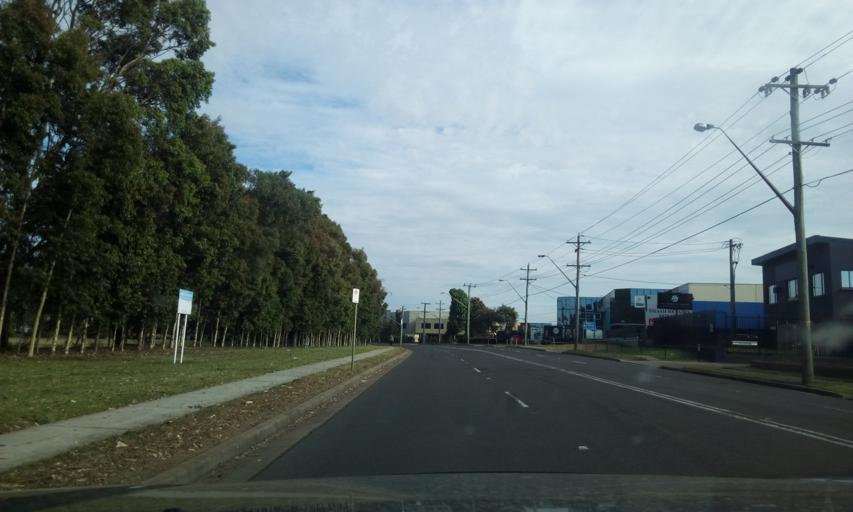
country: AU
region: New South Wales
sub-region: Fairfield
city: Liverpool
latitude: -33.9341
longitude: 150.9347
